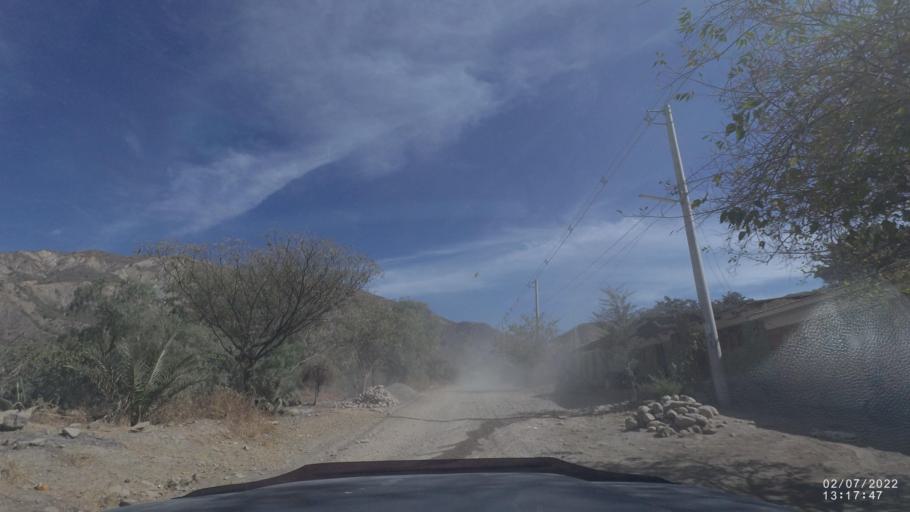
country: BO
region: Cochabamba
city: Irpa Irpa
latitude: -17.7332
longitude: -66.3106
